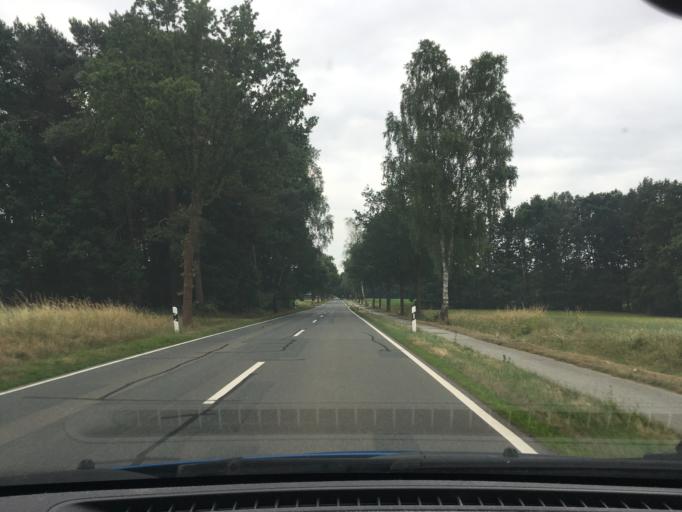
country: DE
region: Lower Saxony
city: Drestedt
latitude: 53.3399
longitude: 9.7558
